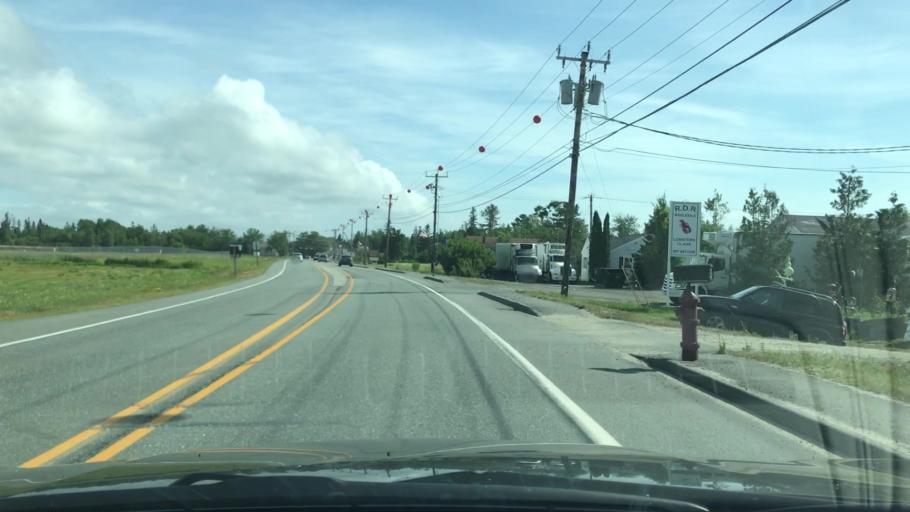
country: US
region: Maine
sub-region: Hancock County
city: Trenton
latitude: 44.4441
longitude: -68.3698
